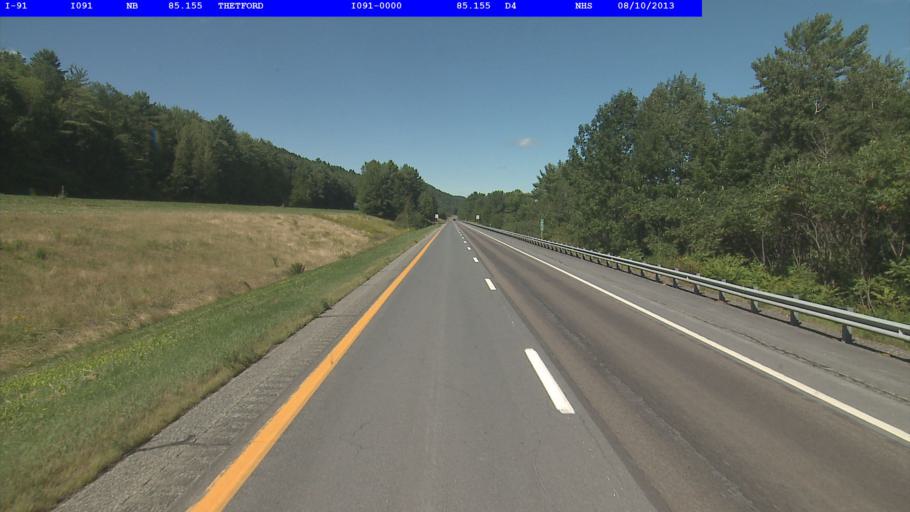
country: US
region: New Hampshire
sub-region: Grafton County
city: Lyme
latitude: 43.8251
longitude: -72.2091
